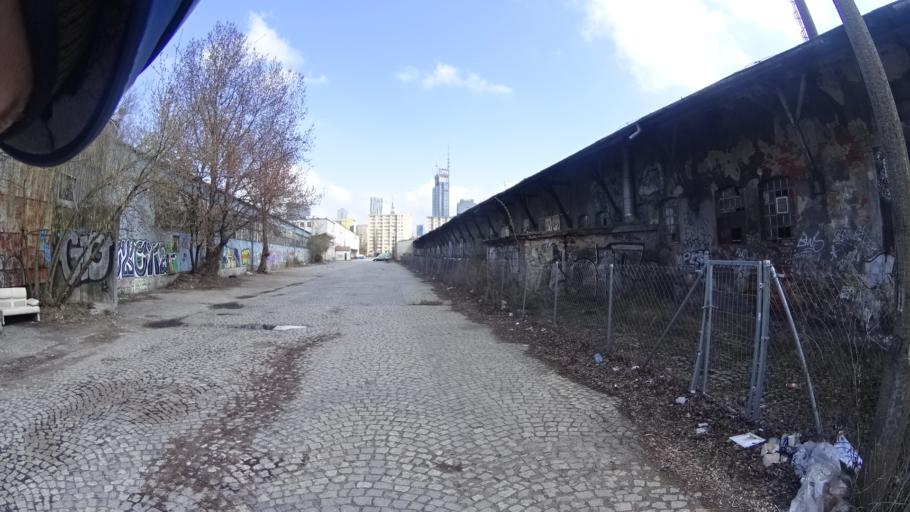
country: PL
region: Masovian Voivodeship
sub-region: Warszawa
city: Ochota
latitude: 52.2257
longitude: 20.9839
